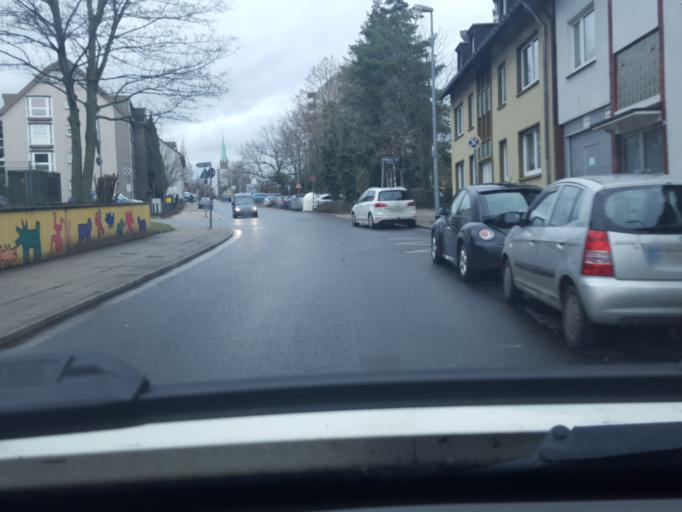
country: DE
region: North Rhine-Westphalia
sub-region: Regierungsbezirk Munster
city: Bottrop
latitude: 51.4704
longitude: 6.9529
